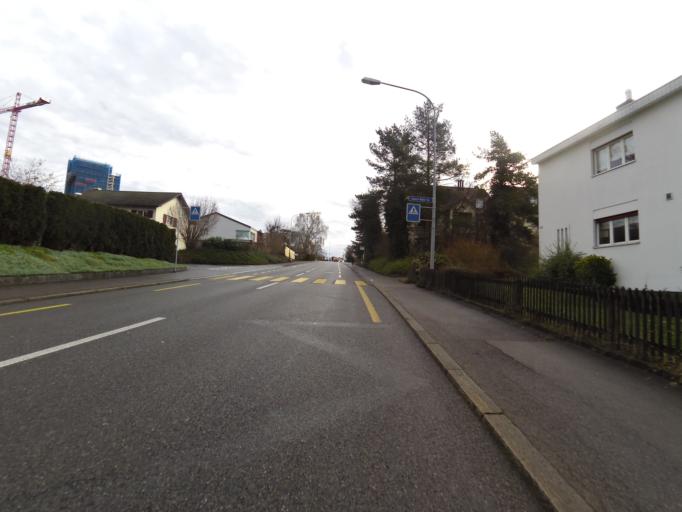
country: CH
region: Thurgau
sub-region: Frauenfeld District
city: Frauenfeld
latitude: 47.5489
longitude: 8.9064
